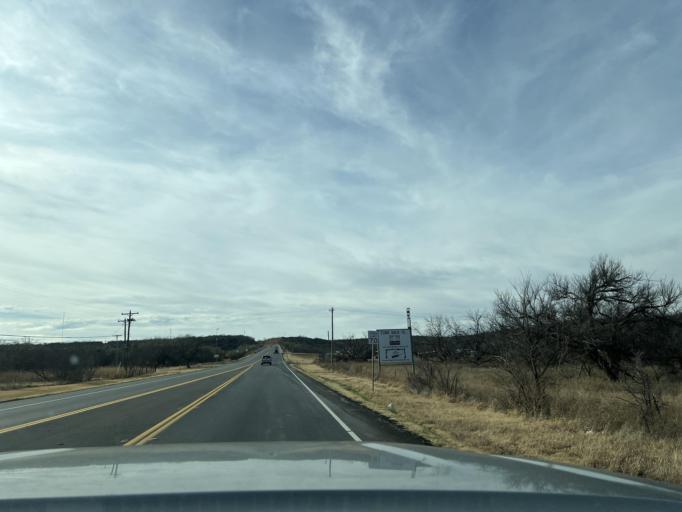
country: US
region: Texas
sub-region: Shackelford County
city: Albany
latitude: 32.7180
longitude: -99.3070
